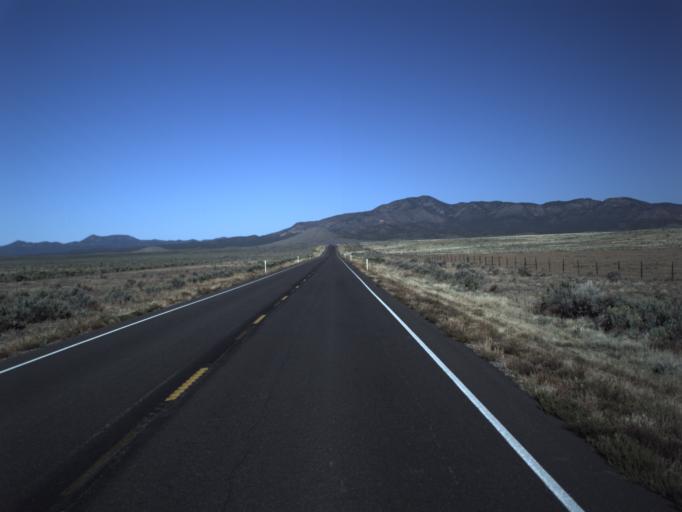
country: US
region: Utah
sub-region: Washington County
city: Enterprise
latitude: 37.7828
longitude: -113.8649
